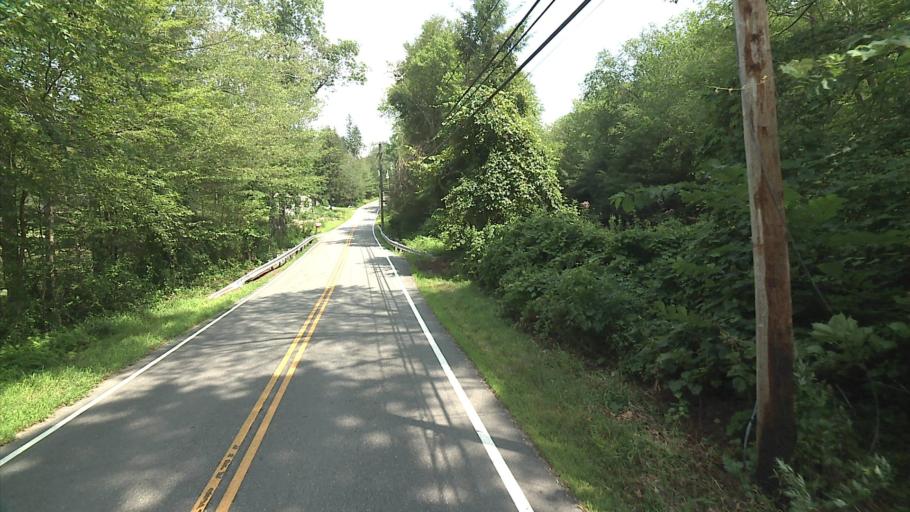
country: US
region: Connecticut
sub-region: Windham County
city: Danielson
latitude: 41.7727
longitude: -71.8432
